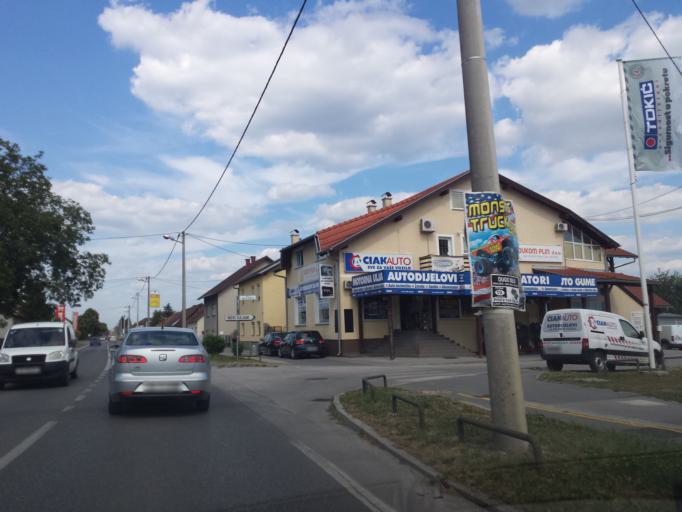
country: HR
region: Zagrebacka
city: Brckovljani
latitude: 45.8046
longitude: 16.2472
